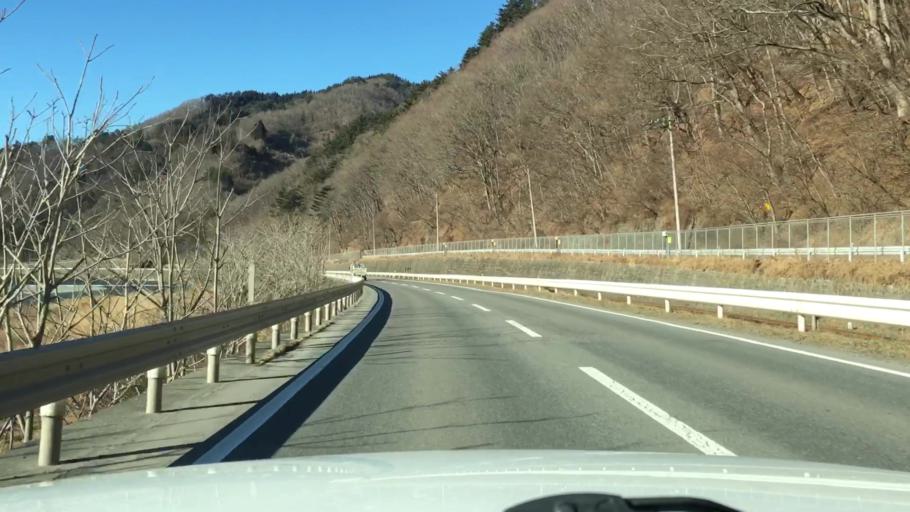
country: JP
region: Iwate
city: Miyako
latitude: 39.6319
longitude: 141.8531
